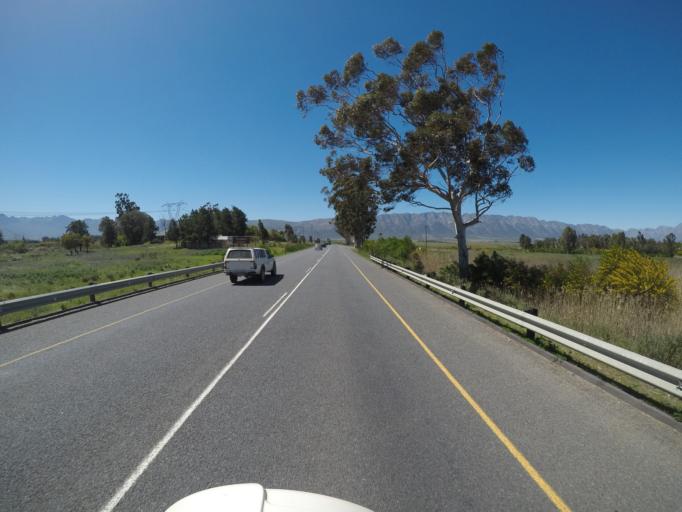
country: ZA
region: Western Cape
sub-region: Cape Winelands District Municipality
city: Ceres
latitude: -33.3100
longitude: 19.1026
